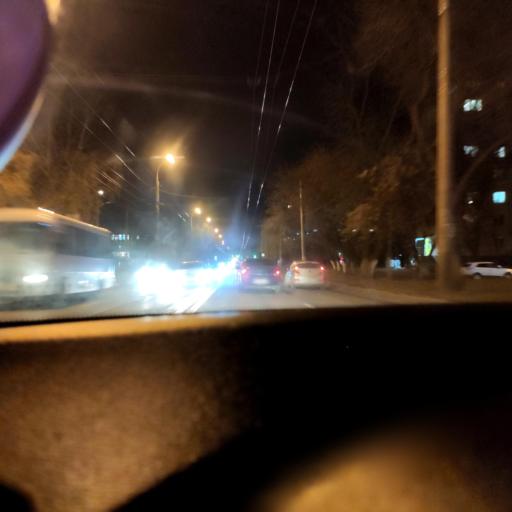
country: RU
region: Samara
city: Samara
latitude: 53.2409
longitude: 50.2353
